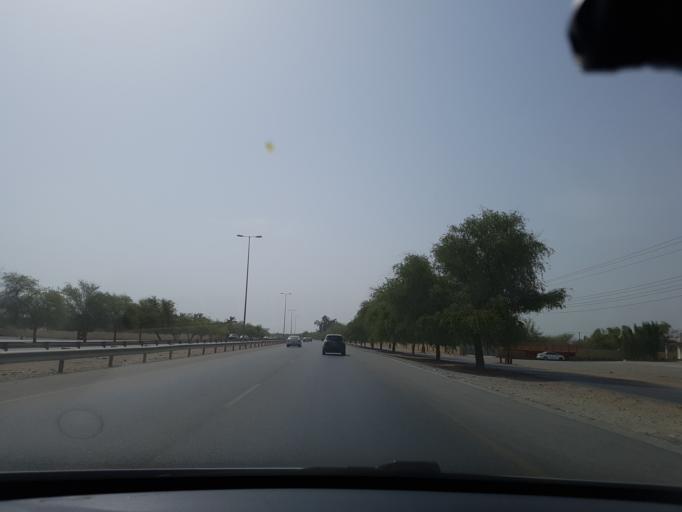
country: OM
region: Al Batinah
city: Al Khaburah
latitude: 23.9501
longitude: 57.1086
